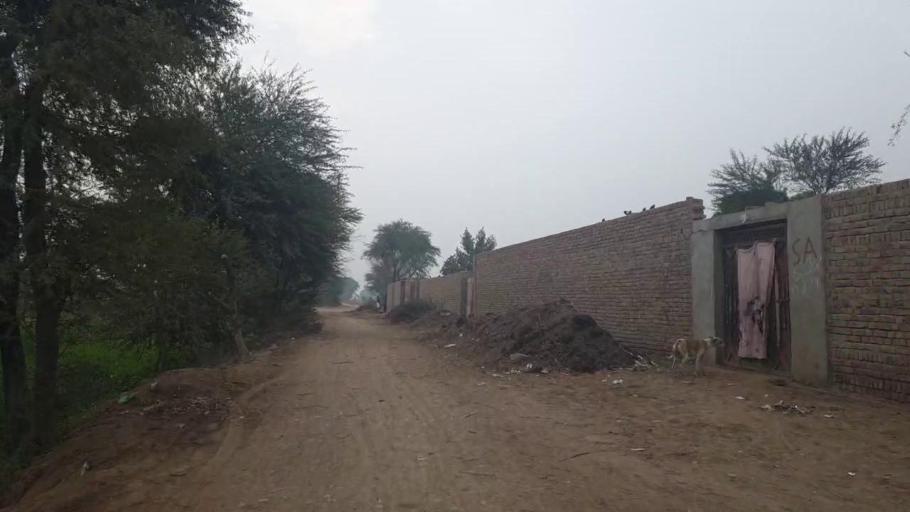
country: PK
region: Sindh
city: Tando Adam
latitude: 25.7102
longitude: 68.6163
